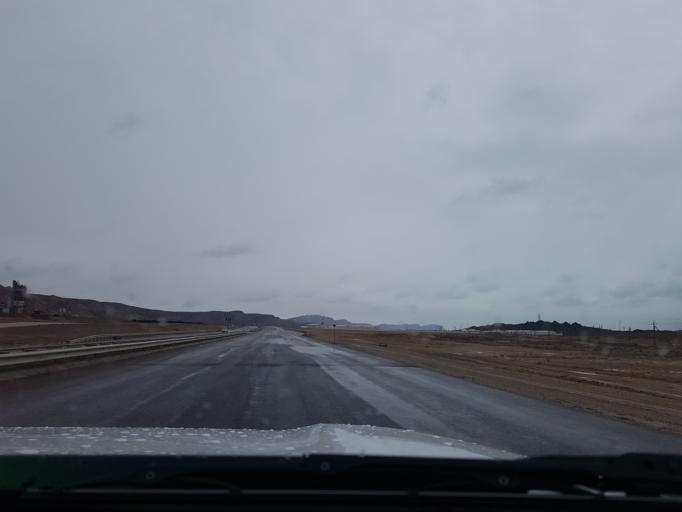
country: TM
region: Balkan
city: Turkmenbasy
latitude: 40.0140
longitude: 53.0854
